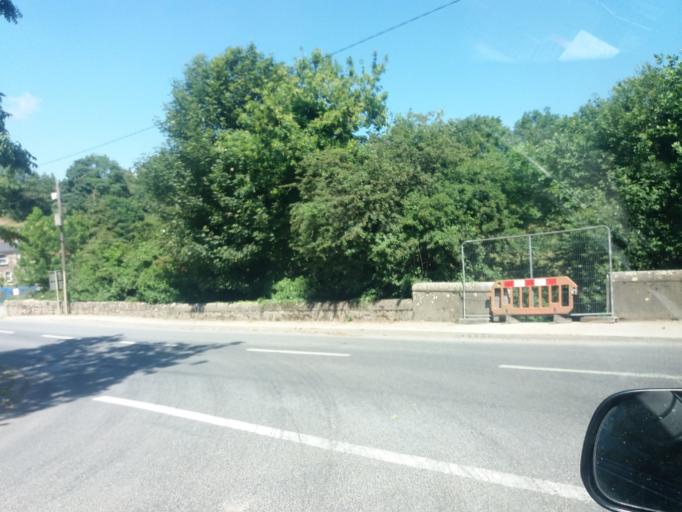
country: IE
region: Leinster
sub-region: An Mhi
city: Stamullin
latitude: 53.5876
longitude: -6.2919
